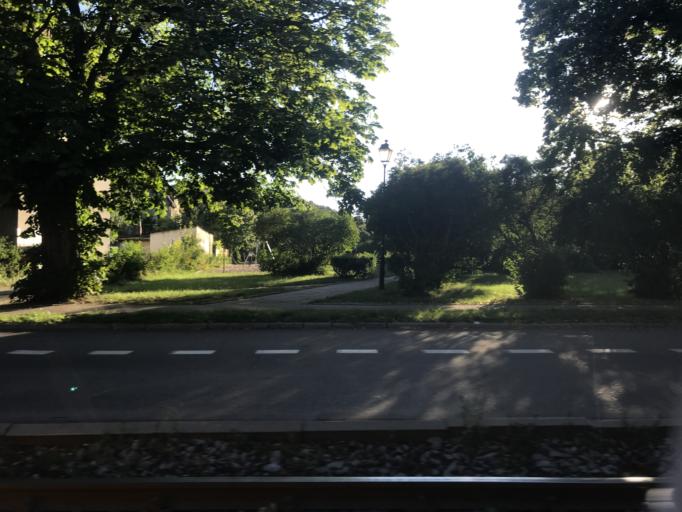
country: PL
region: Pomeranian Voivodeship
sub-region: Sopot
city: Sopot
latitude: 54.4065
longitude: 18.5635
